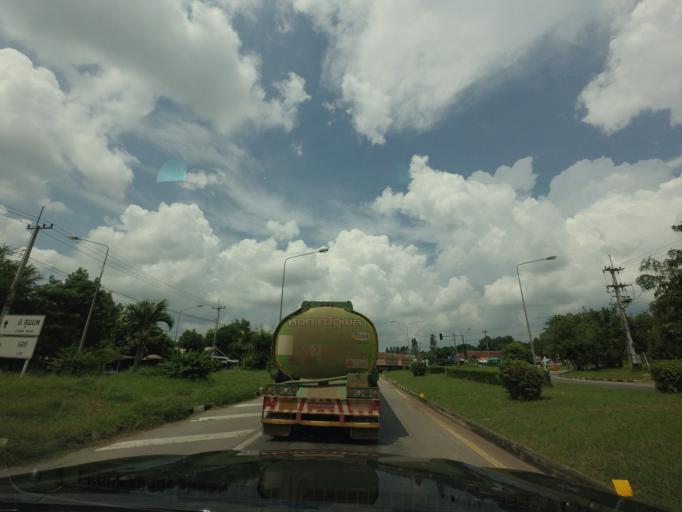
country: TH
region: Khon Kaen
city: Nong Ruea
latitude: 16.4883
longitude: 102.4065
